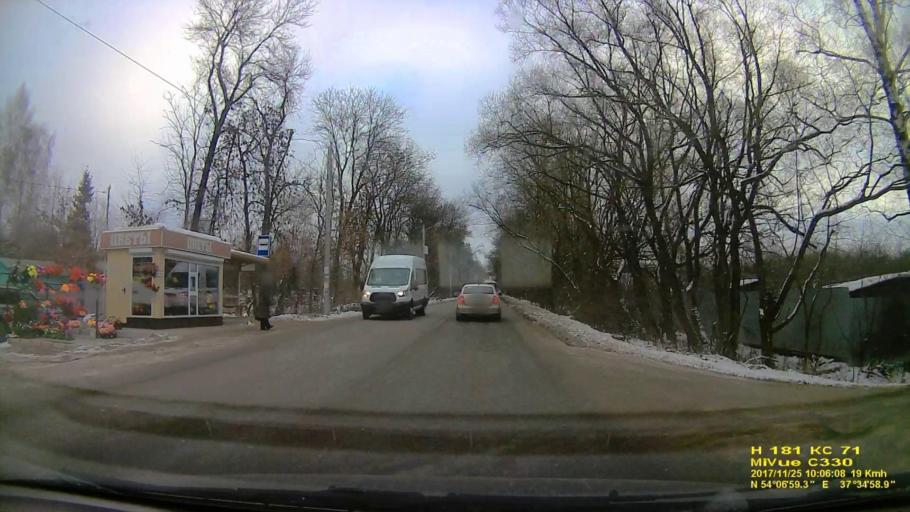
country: RU
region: Tula
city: Mendeleyevskiy
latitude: 54.1165
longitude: 37.5831
